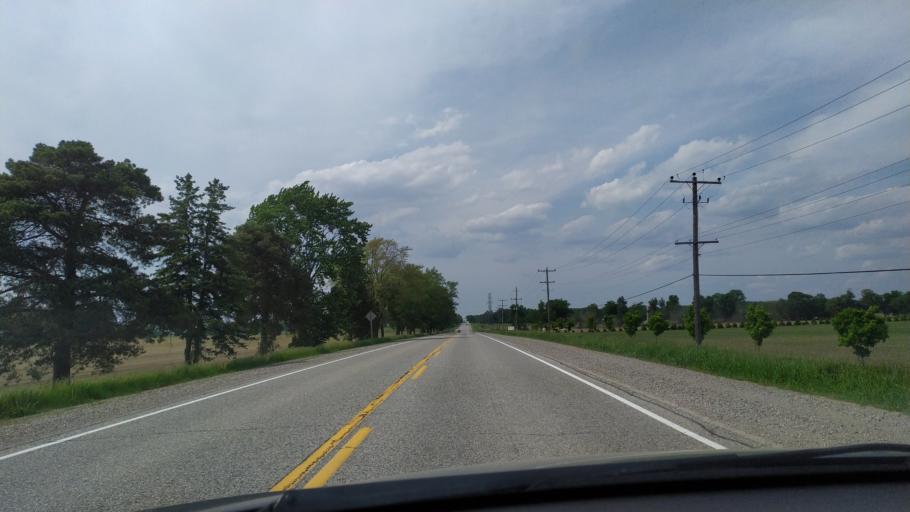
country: CA
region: Ontario
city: Dorchester
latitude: 43.0819
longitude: -81.0009
